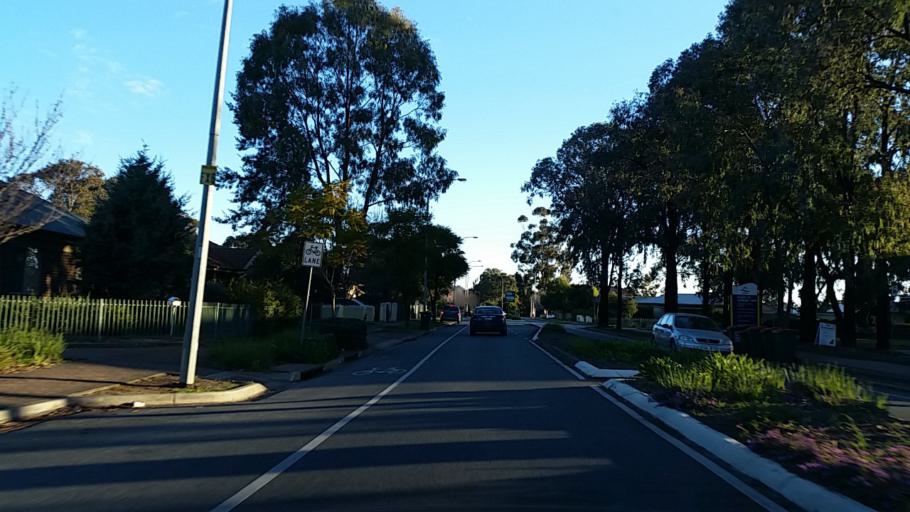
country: AU
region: South Australia
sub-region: Salisbury
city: Salisbury
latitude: -34.7546
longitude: 138.6324
